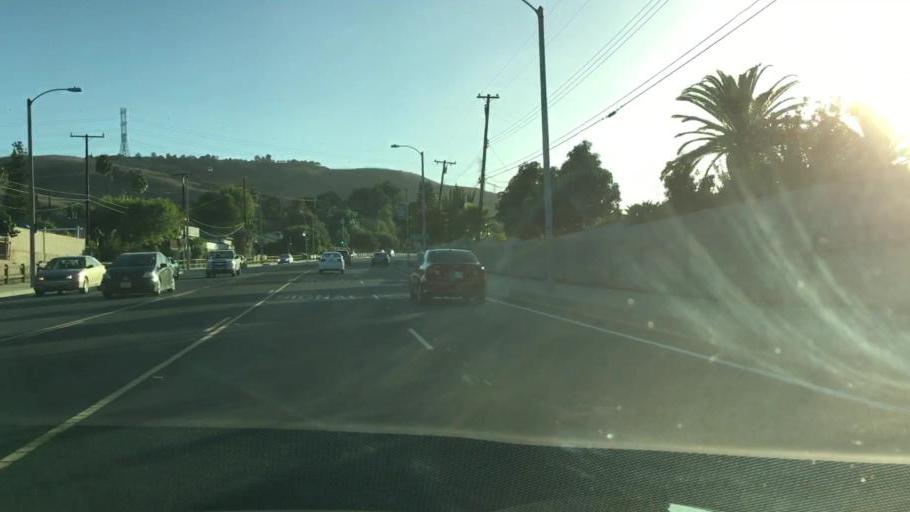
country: US
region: California
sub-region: Los Angeles County
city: Rowland Heights
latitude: 33.9722
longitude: -117.8949
